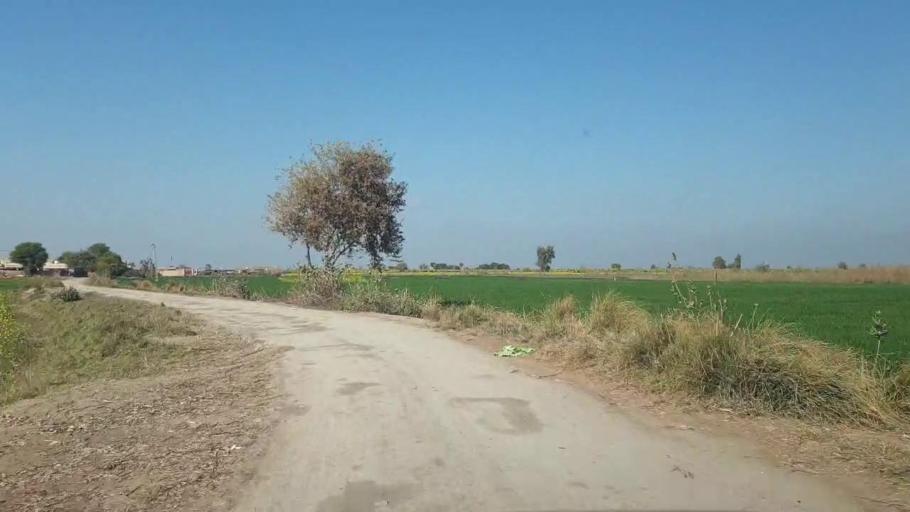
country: PK
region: Sindh
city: Shahdadpur
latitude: 25.9232
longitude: 68.5643
